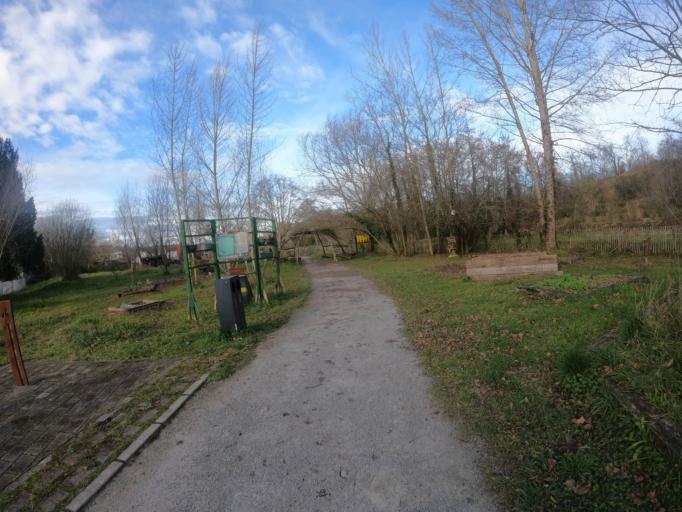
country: FR
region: Aquitaine
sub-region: Departement des Pyrenees-Atlantiques
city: Jurancon
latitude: 43.2937
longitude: -0.3831
